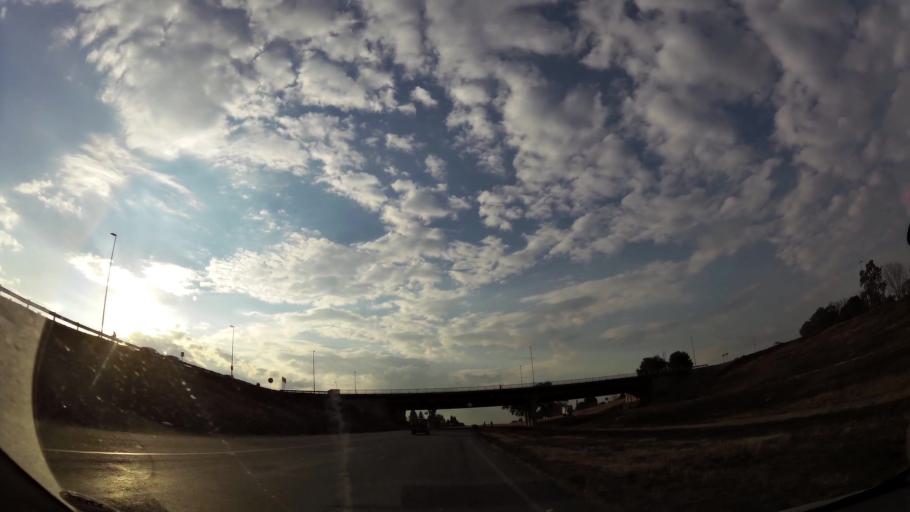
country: ZA
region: Gauteng
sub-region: Sedibeng District Municipality
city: Vanderbijlpark
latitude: -26.7387
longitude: 27.8230
